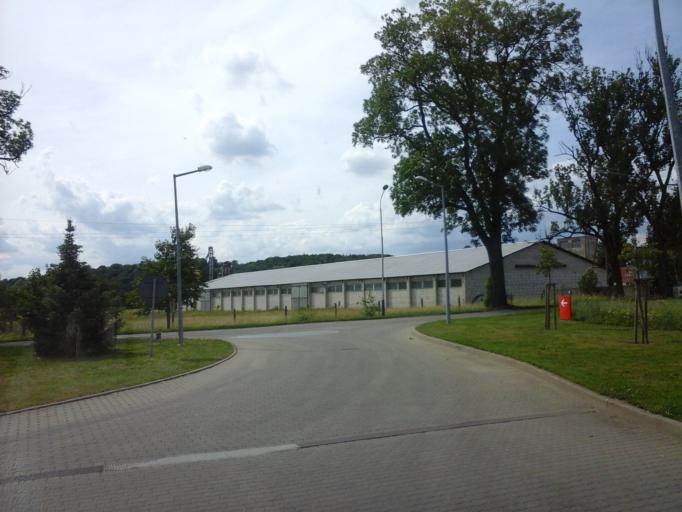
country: PL
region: West Pomeranian Voivodeship
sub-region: Powiat lobeski
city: Lobez
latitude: 53.6223
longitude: 15.6127
